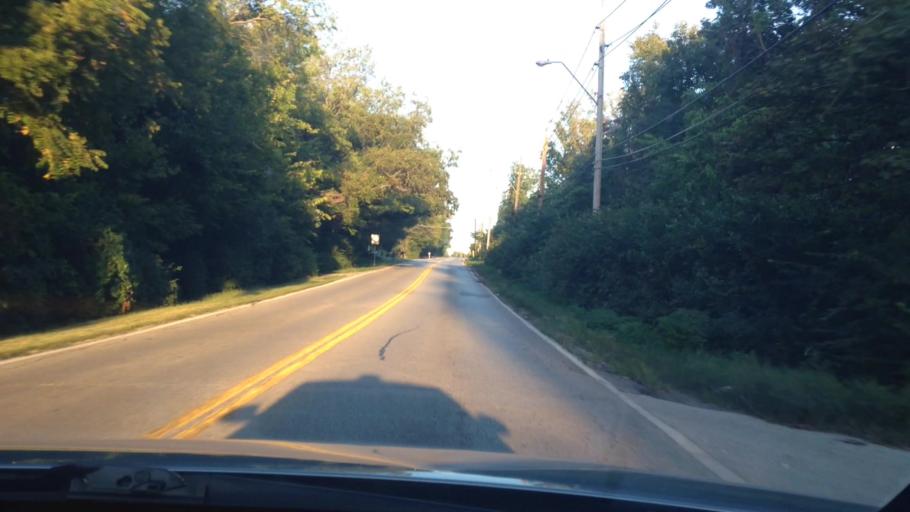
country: US
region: Missouri
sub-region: Jackson County
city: Grandview
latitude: 38.9250
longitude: -94.5633
